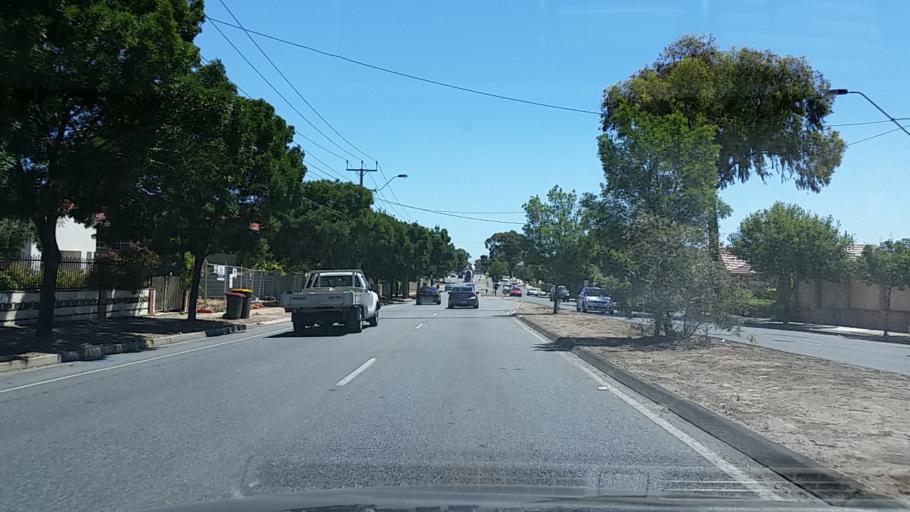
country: AU
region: South Australia
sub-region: Campbelltown
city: Hectorville
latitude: -34.8915
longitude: 138.6515
